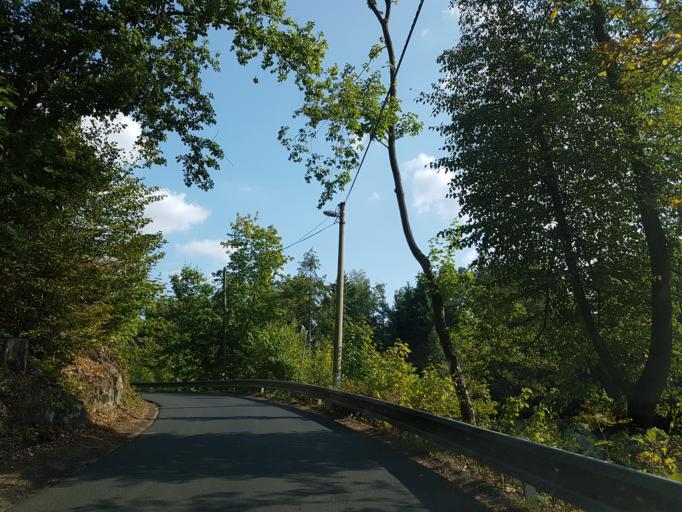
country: CZ
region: Ustecky
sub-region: Okres Decin
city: Decin
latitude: 50.8625
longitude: 14.2603
